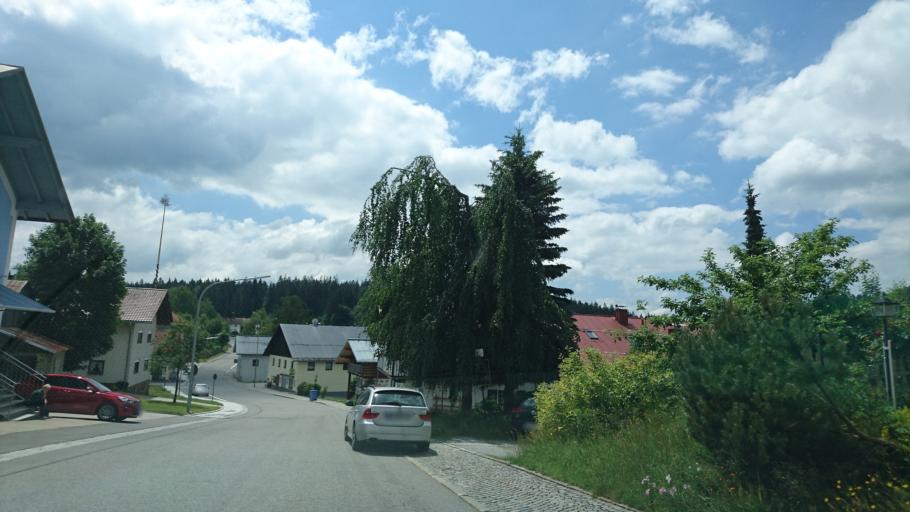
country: DE
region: Bavaria
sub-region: Lower Bavaria
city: Mauth
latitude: 48.8880
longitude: 13.5839
